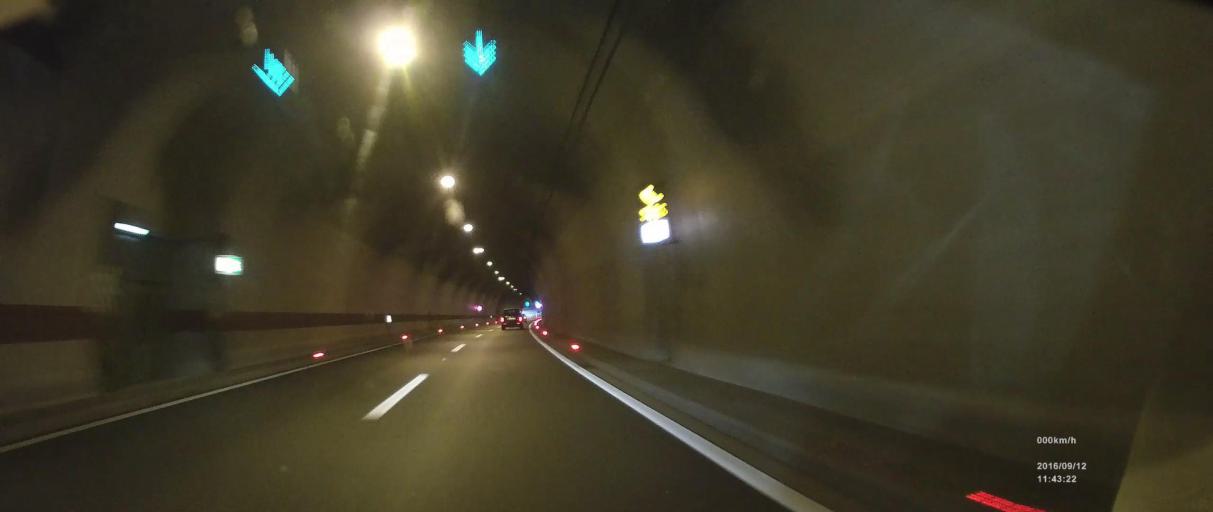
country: HR
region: Licko-Senjska
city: Brinje
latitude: 44.9793
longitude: 15.0925
